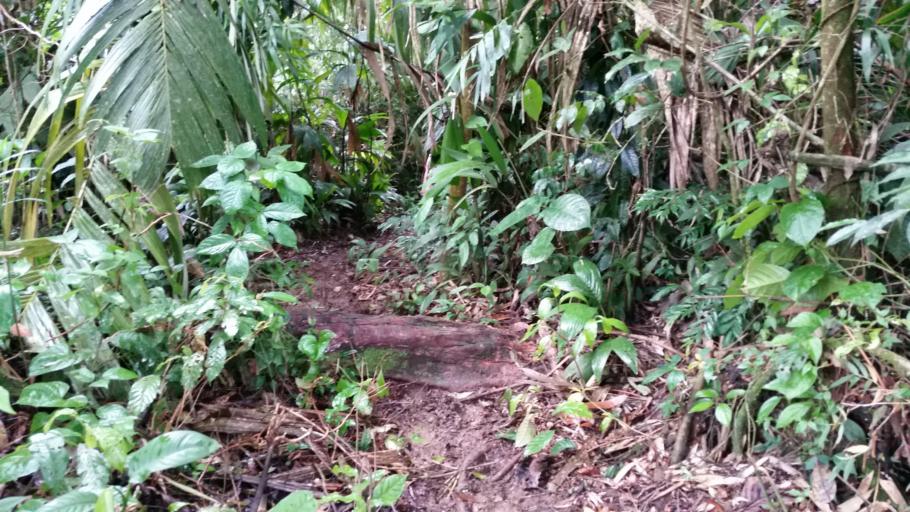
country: NI
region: Atlantico Norte (RAAN)
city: Bonanza
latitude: 14.0926
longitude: -84.6769
